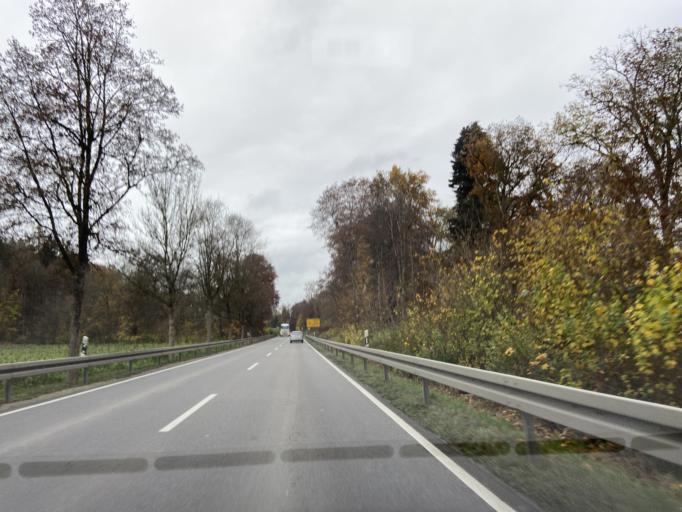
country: DE
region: Baden-Wuerttemberg
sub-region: Tuebingen Region
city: Krauchenwies
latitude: 48.0248
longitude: 9.2488
